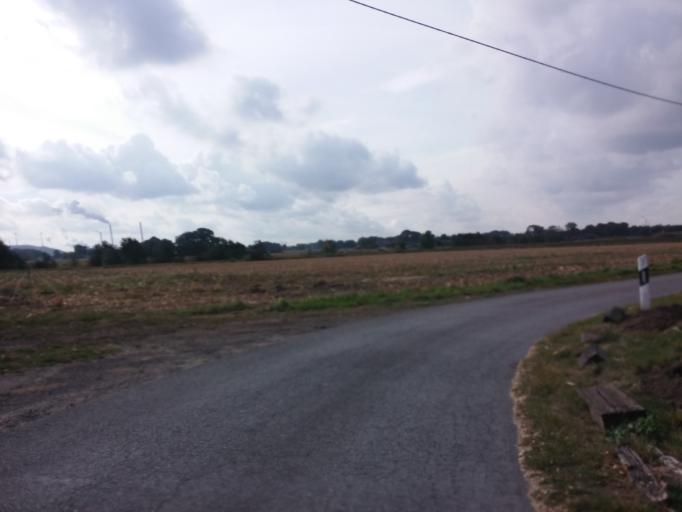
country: DE
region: North Rhine-Westphalia
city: Dorsten
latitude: 51.6470
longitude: 7.0148
